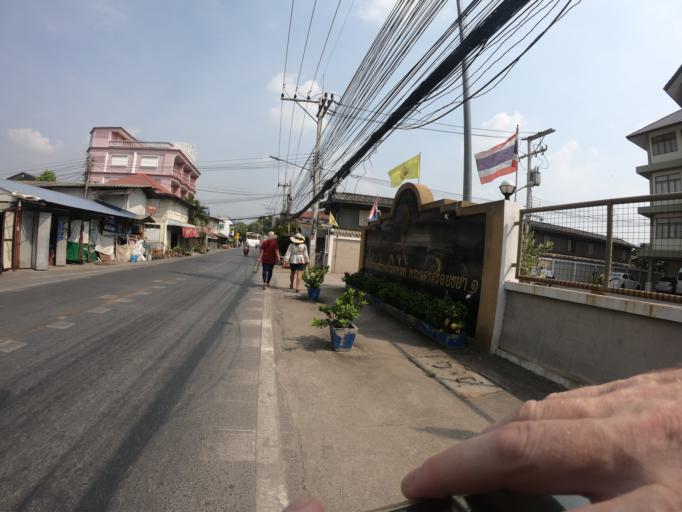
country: TH
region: Phra Nakhon Si Ayutthaya
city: Phra Nakhon Si Ayutthaya
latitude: 14.3464
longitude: 100.5779
